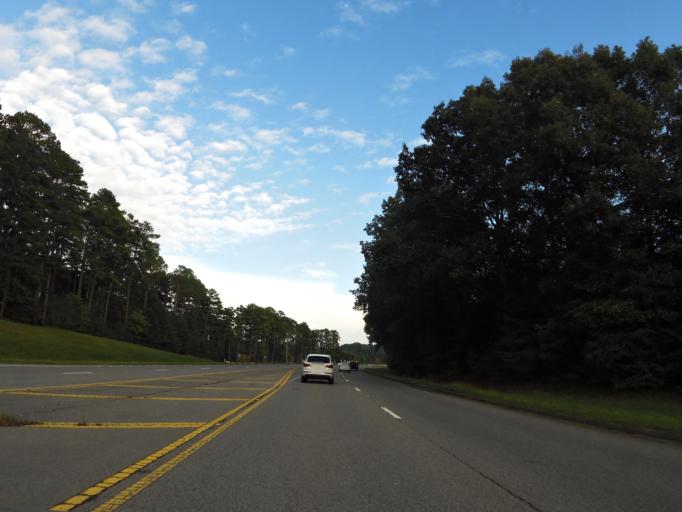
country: US
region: Alabama
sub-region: Lauderdale County
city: Rogersville
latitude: 34.8090
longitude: -87.2372
